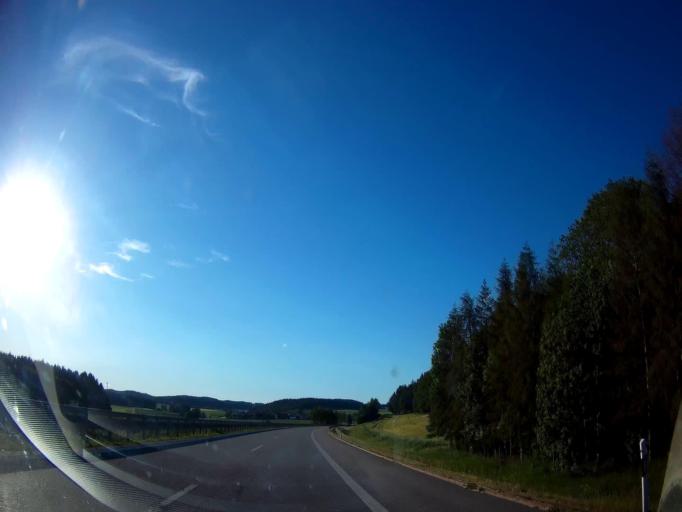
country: DE
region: Bavaria
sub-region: Upper Palatinate
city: Hohenfels
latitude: 49.1533
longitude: 11.8405
